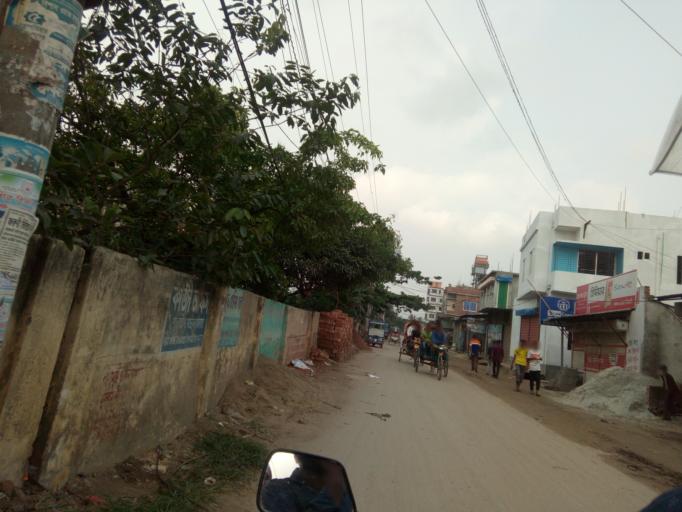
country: BD
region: Dhaka
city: Paltan
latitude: 23.7153
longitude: 90.4608
